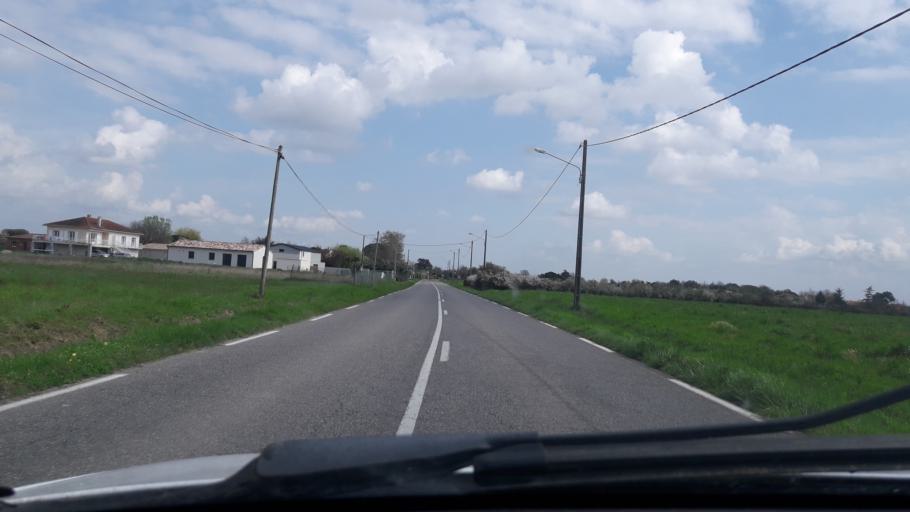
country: FR
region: Midi-Pyrenees
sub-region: Departement de la Haute-Garonne
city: Seysses
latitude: 43.4999
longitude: 1.2867
